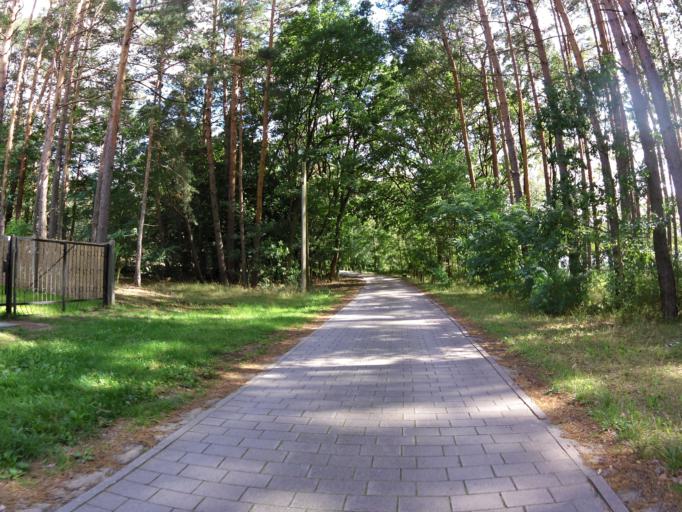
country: DE
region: Brandenburg
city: Munchehofe
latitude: 52.1880
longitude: 13.8822
